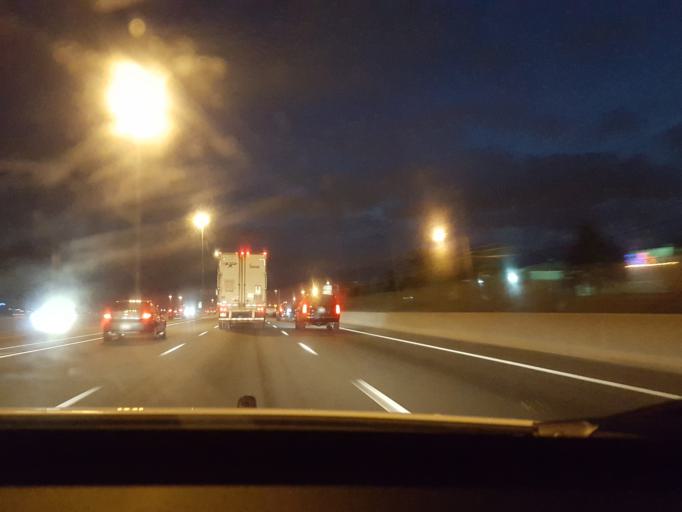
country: CA
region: Ontario
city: Burlington
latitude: 43.3741
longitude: -79.7797
